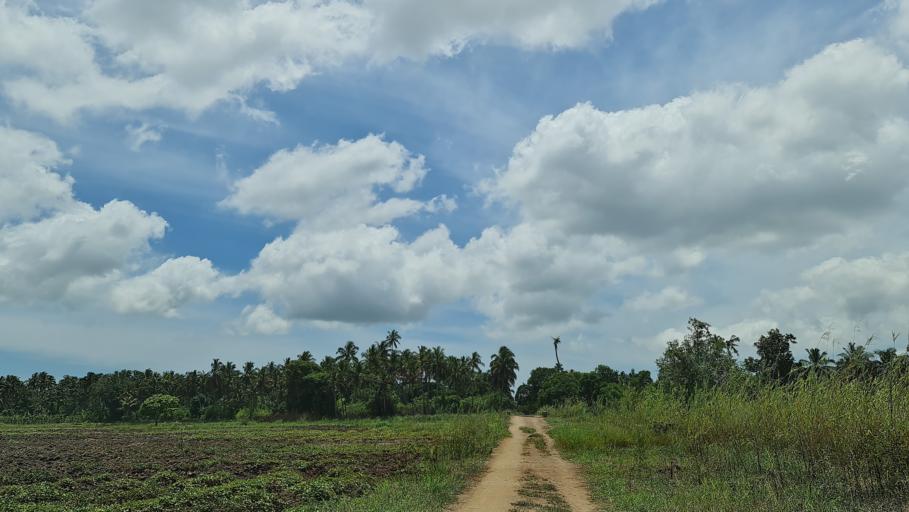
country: MZ
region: Zambezia
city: Quelimane
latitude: -17.5748
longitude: 37.3741
